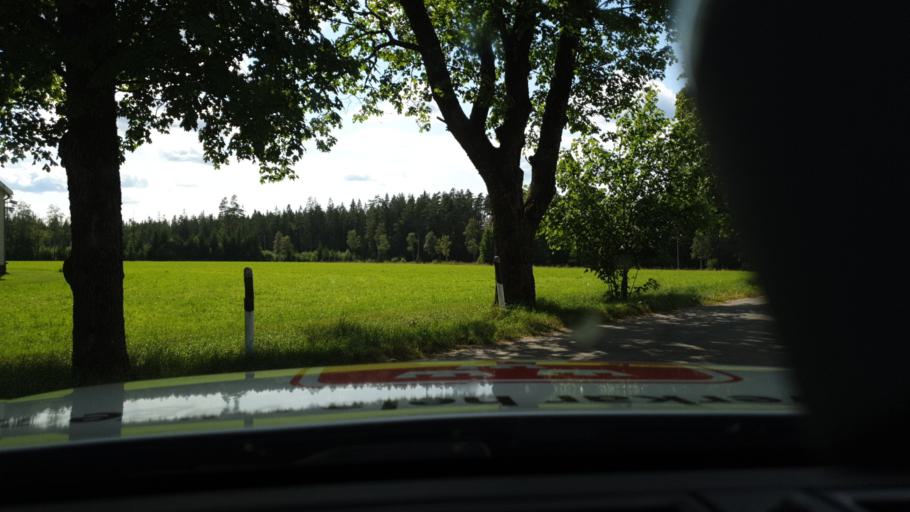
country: SE
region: Joenkoeping
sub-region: Gnosjo Kommun
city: Marieholm
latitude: 57.5610
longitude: 13.9127
